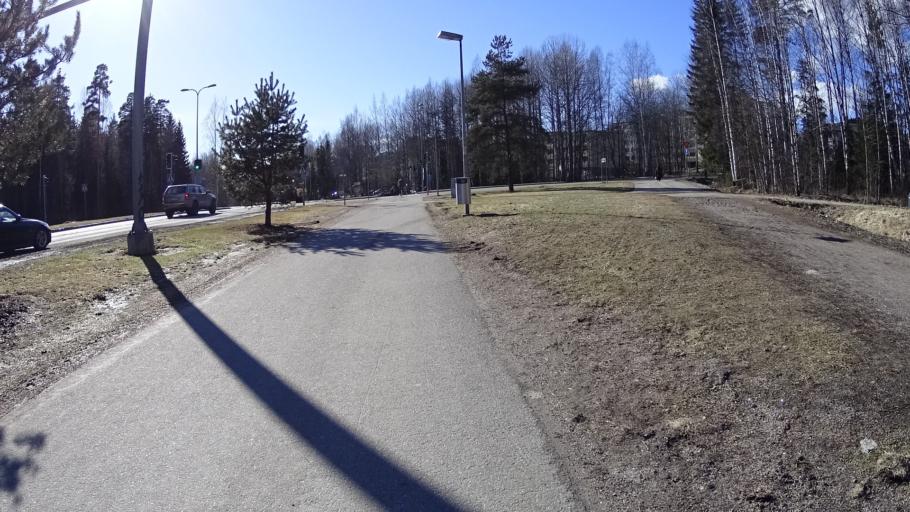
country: FI
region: Uusimaa
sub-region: Helsinki
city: Kilo
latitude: 60.2593
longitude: 24.8362
